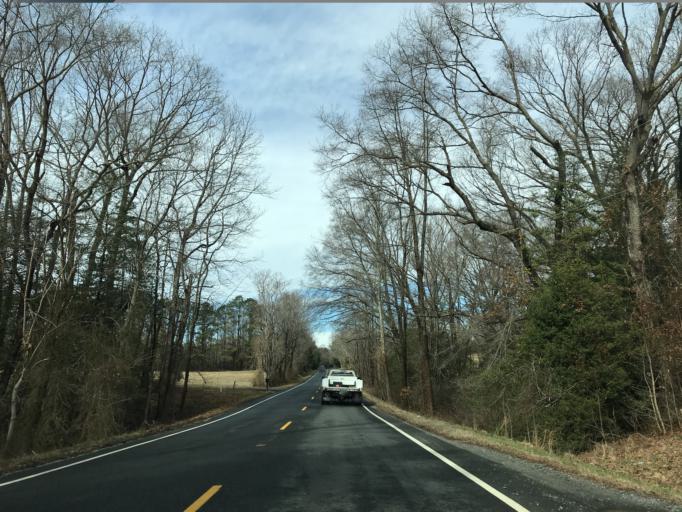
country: US
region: Virginia
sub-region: King George County
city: Dahlgren
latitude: 38.2894
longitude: -77.0602
